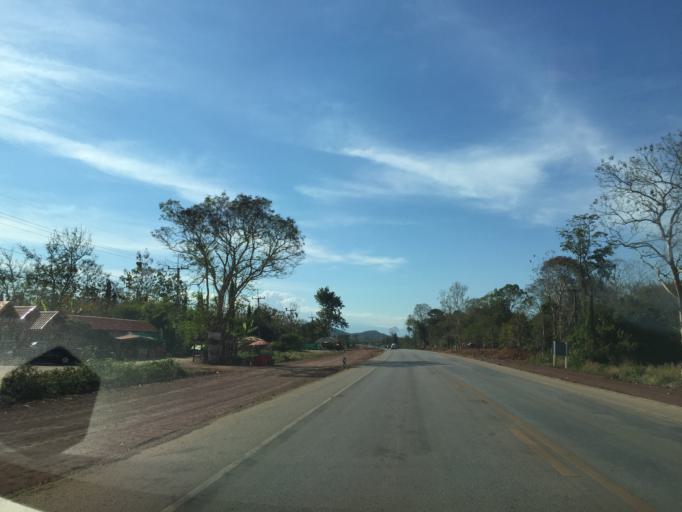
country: TH
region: Loei
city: Erawan
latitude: 17.2984
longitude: 101.8695
